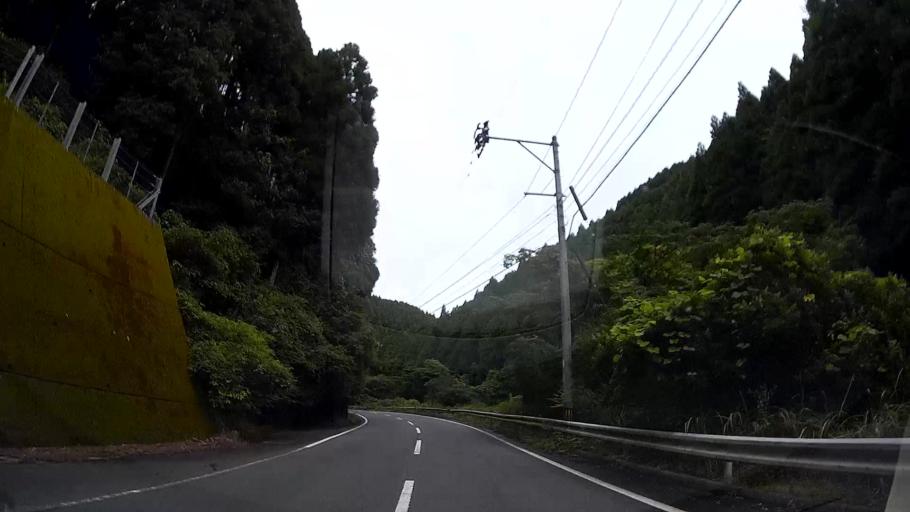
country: JP
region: Kumamoto
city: Kikuchi
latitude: 33.0335
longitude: 130.8916
